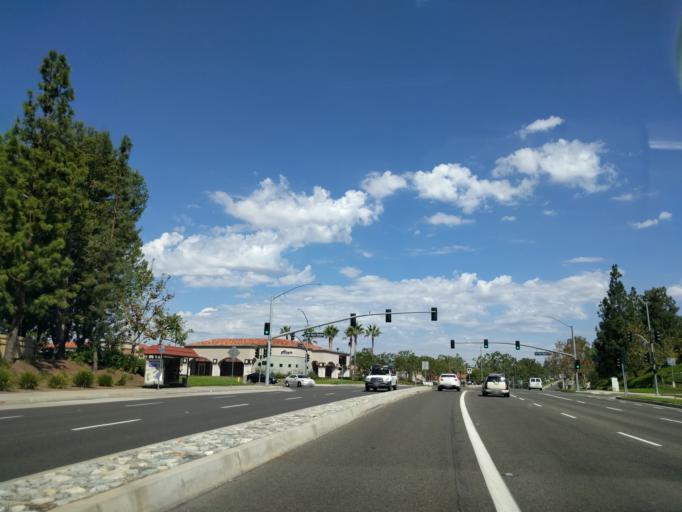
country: US
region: California
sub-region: Orange County
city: Laguna Niguel
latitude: 33.5217
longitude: -117.6857
